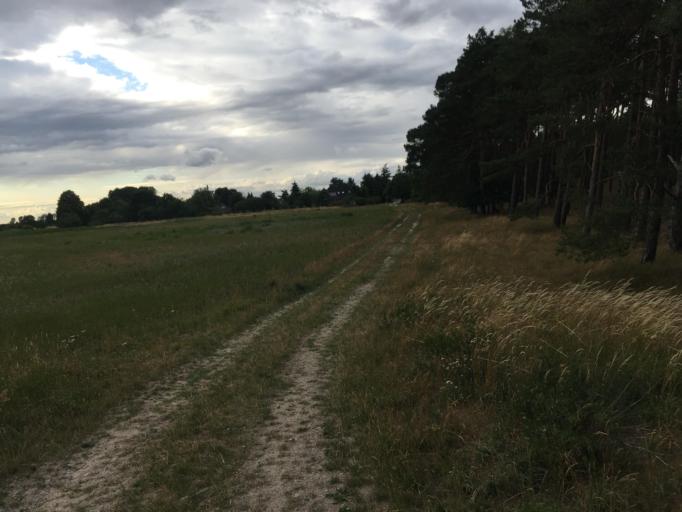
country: DE
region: Lower Saxony
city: Neu Darchau
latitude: 53.2737
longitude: 10.9397
